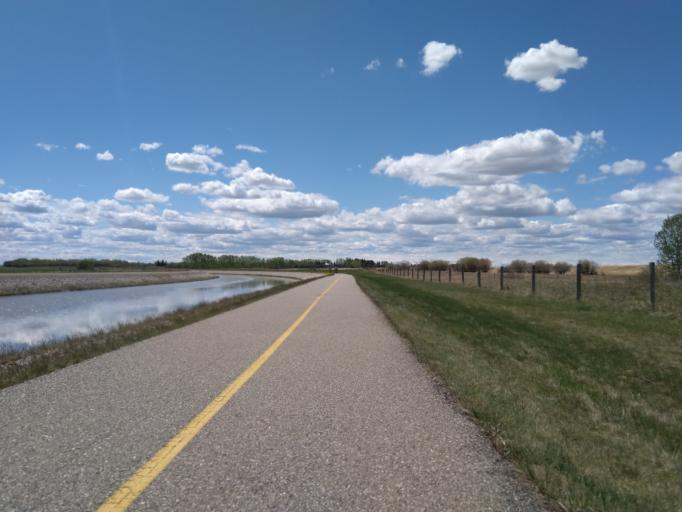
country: CA
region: Alberta
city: Chestermere
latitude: 51.0042
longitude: -113.8544
